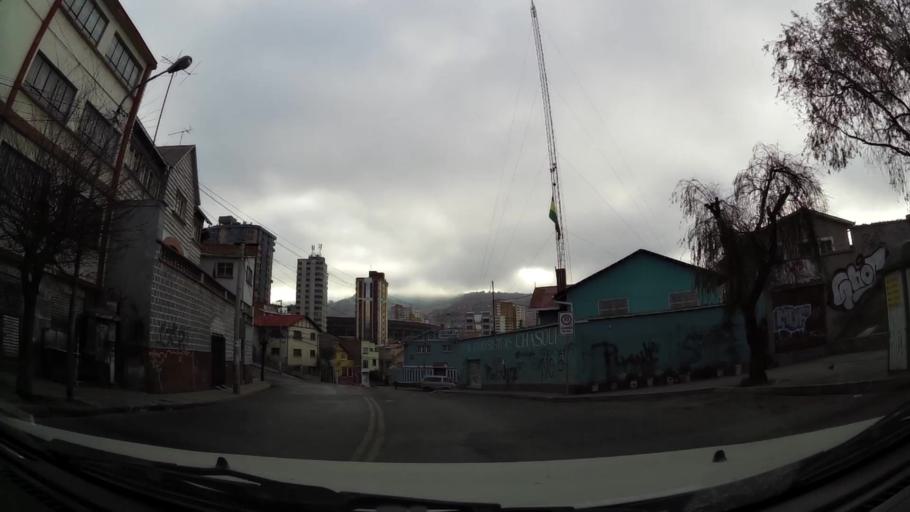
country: BO
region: La Paz
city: La Paz
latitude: -16.5021
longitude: -68.1244
